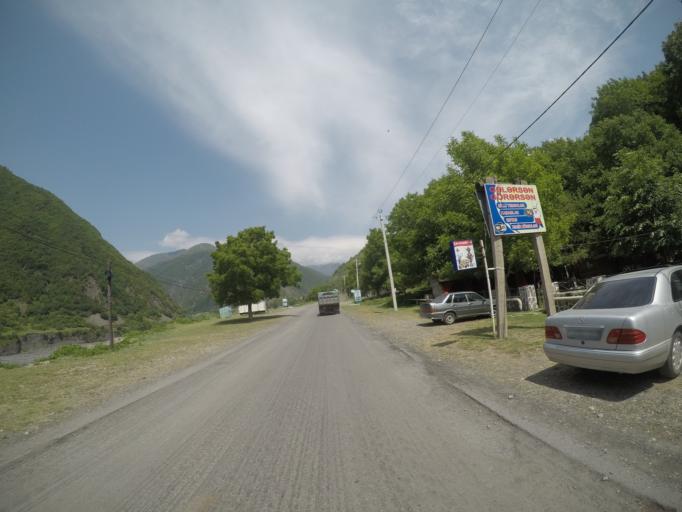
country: AZ
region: Qakh Rayon
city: Qaxbas
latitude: 41.4655
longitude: 47.0441
